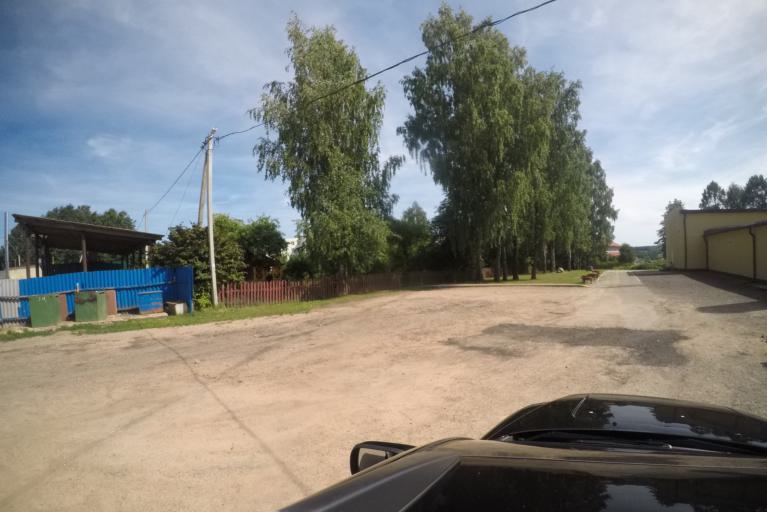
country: BY
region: Grodnenskaya
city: Hal'shany
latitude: 54.2577
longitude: 26.0168
